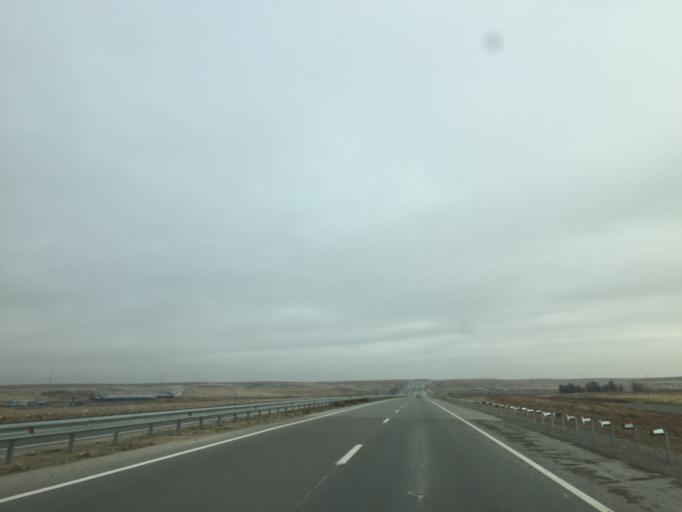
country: KZ
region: Ongtustik Qazaqstan
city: Aksu
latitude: 42.4377
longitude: 69.7208
